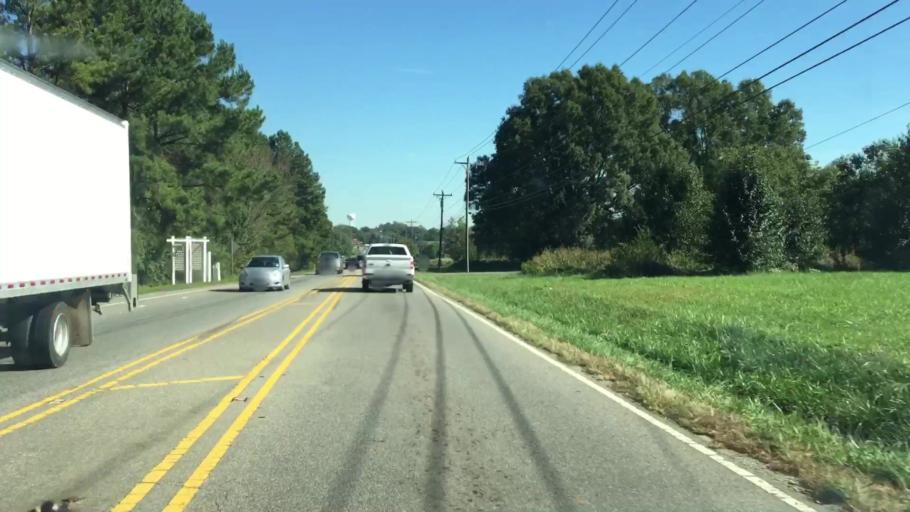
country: US
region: North Carolina
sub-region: Catawba County
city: Lake Norman of Catawba
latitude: 35.5989
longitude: -80.8890
